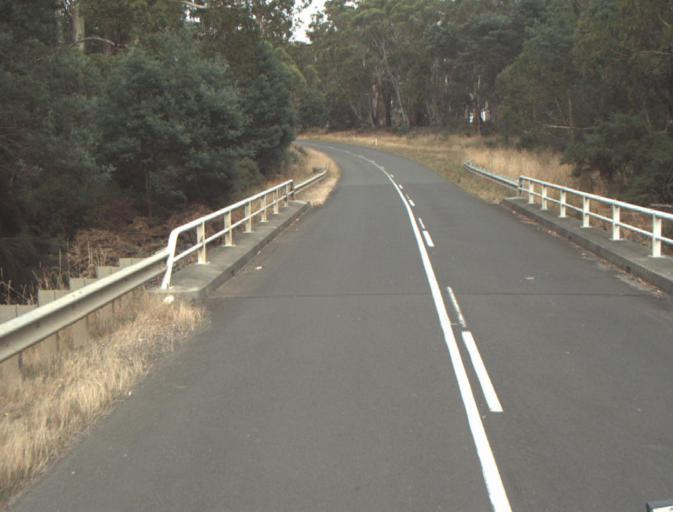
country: AU
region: Tasmania
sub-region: Northern Midlands
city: Evandale
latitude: -41.4891
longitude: 147.5023
